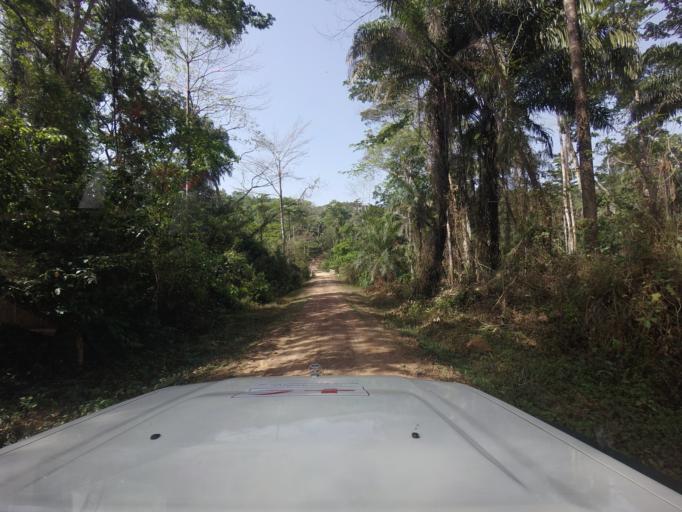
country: LR
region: Lofa
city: Voinjama
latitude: 8.5193
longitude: -9.7598
